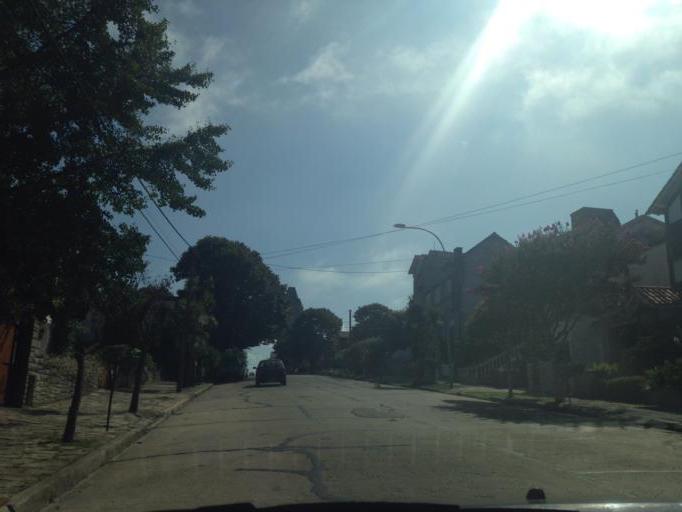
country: AR
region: Buenos Aires
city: Mar del Plata
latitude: -38.0154
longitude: -57.5374
